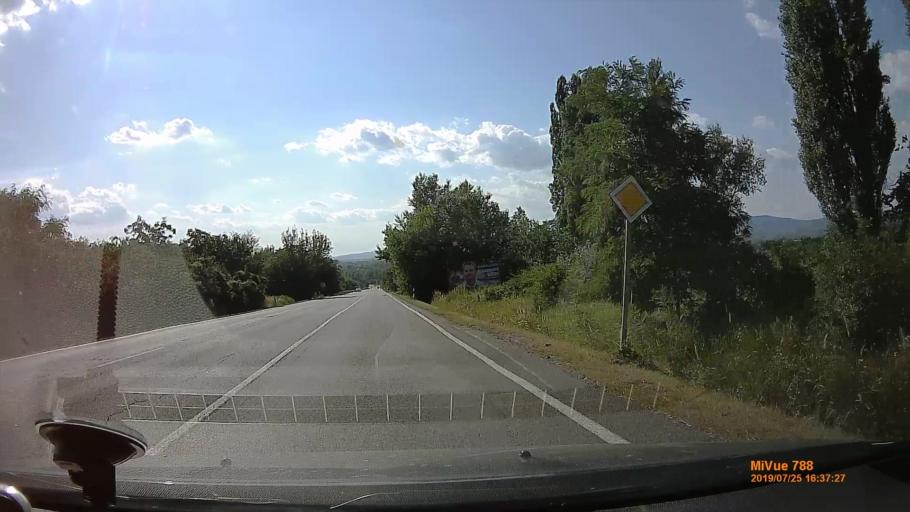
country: HU
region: Heves
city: Gyongyos
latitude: 47.7722
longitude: 19.9605
